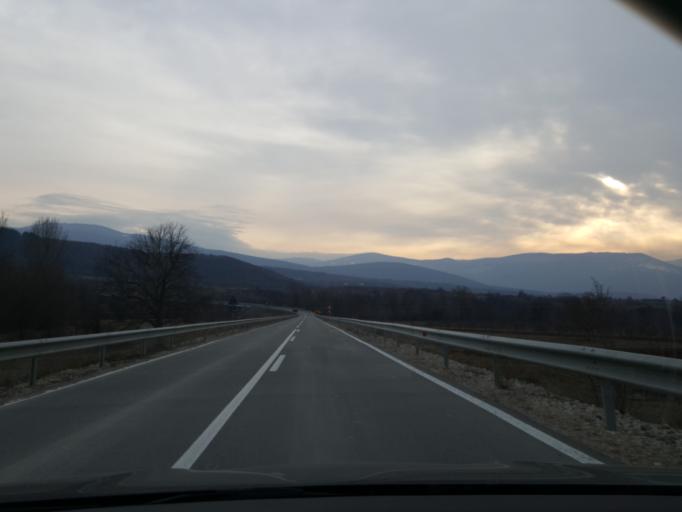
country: RS
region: Central Serbia
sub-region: Pirotski Okrug
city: Bela Palanka
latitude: 43.2333
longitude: 22.3935
